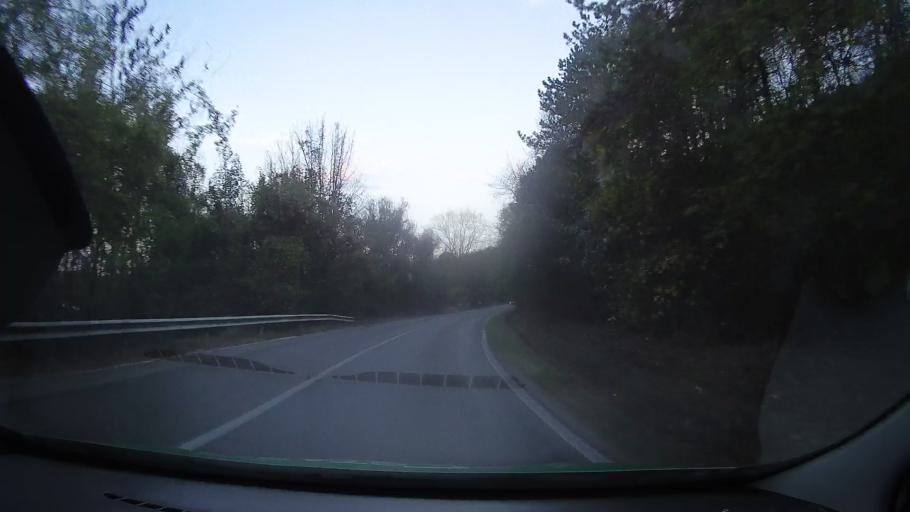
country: RO
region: Constanta
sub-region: Comuna Lipnita
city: Lipnita
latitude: 44.0953
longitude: 27.6474
